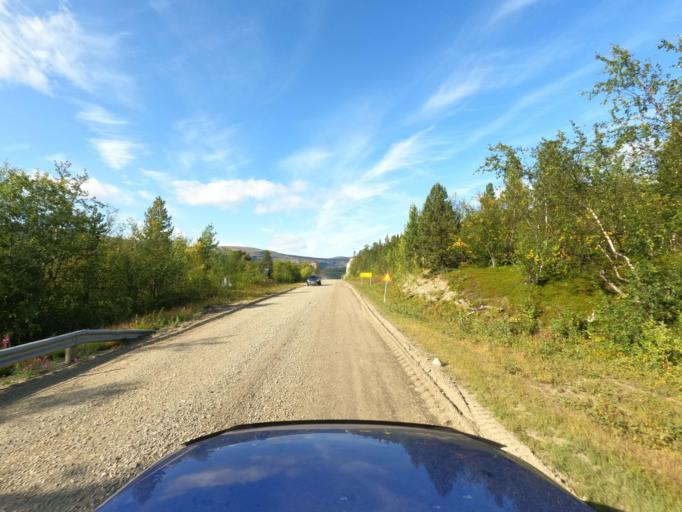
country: NO
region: Finnmark Fylke
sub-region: Porsanger
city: Lakselv
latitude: 69.8892
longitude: 25.0063
